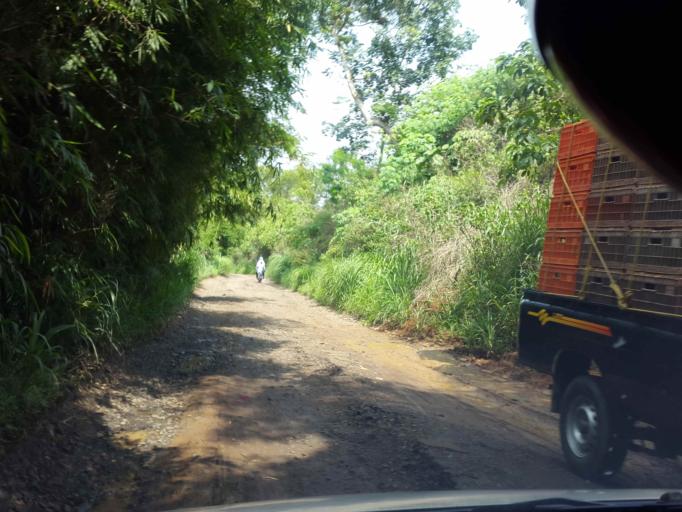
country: ID
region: West Java
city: Legok
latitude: -6.9833
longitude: 106.9714
